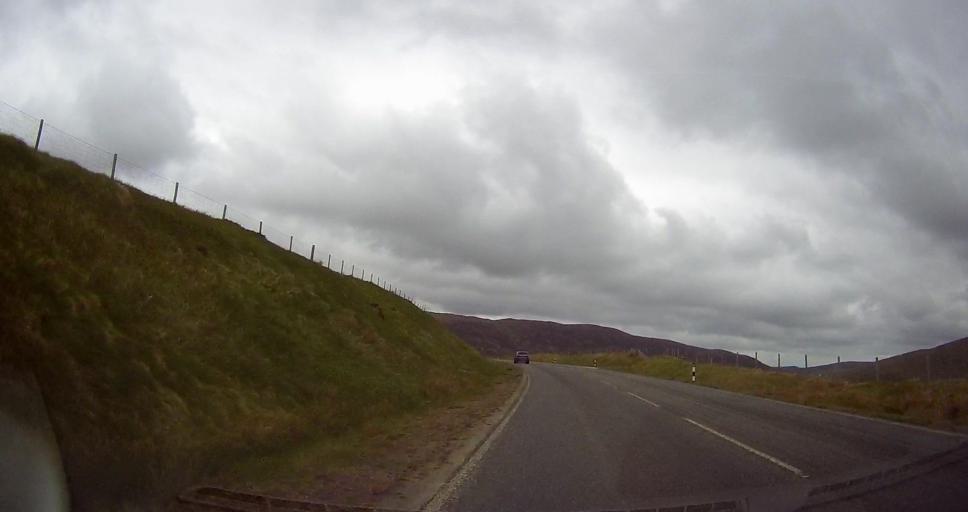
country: GB
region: Scotland
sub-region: Shetland Islands
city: Lerwick
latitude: 60.3707
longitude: -1.3299
